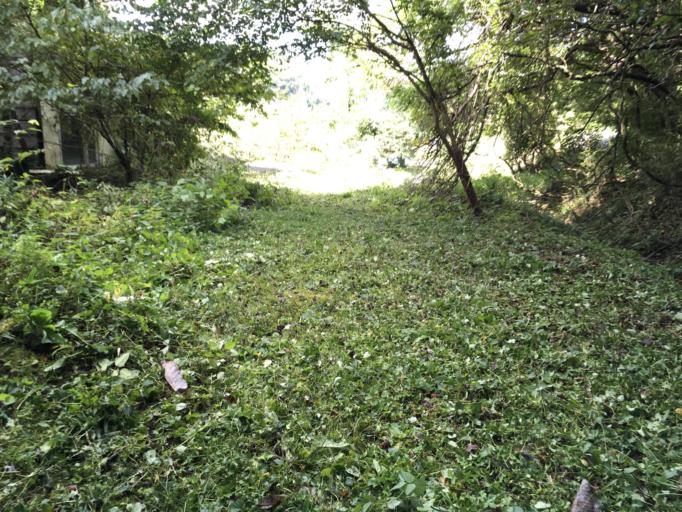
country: JP
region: Iwate
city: Ichinoseki
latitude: 38.8922
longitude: 141.1245
